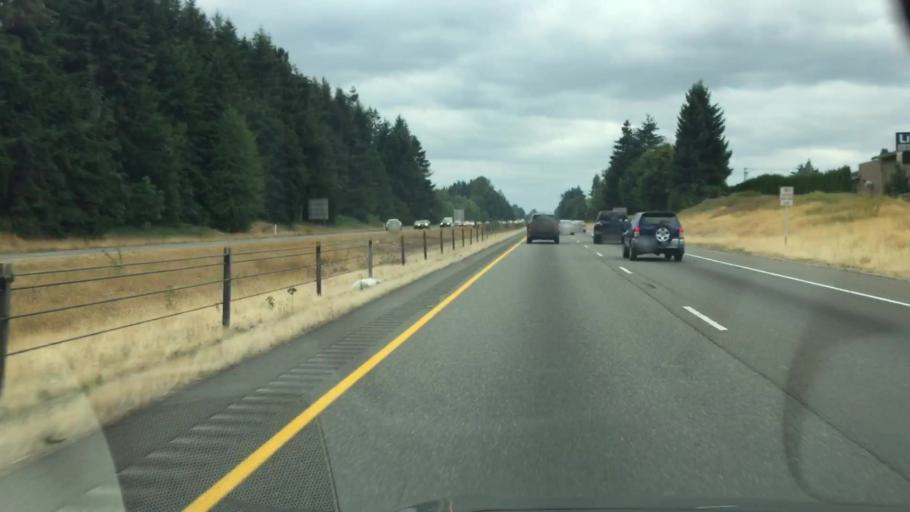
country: US
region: Washington
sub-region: Pierce County
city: Summit
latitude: 47.1586
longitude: -122.3200
